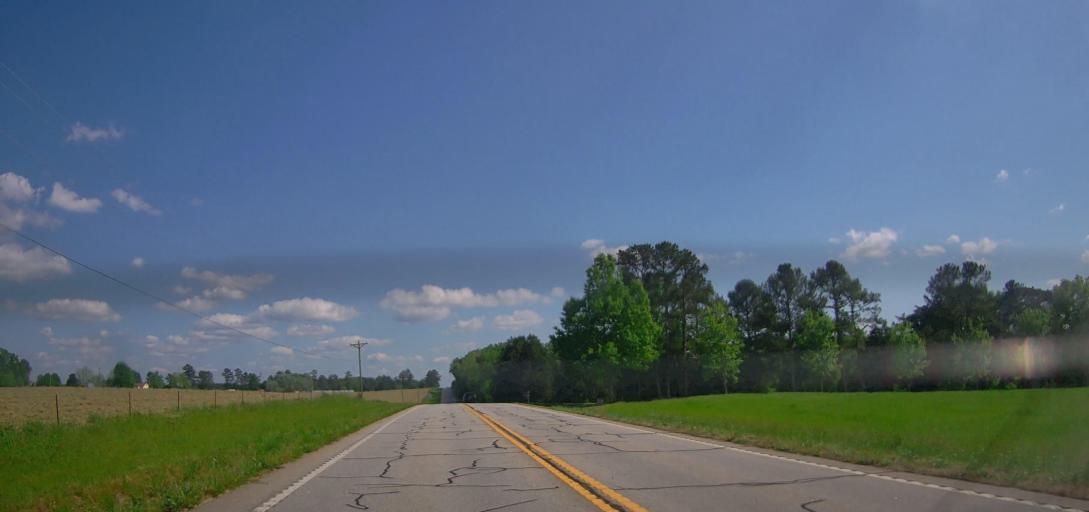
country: US
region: Georgia
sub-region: Greene County
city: Greensboro
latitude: 33.6105
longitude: -83.3117
